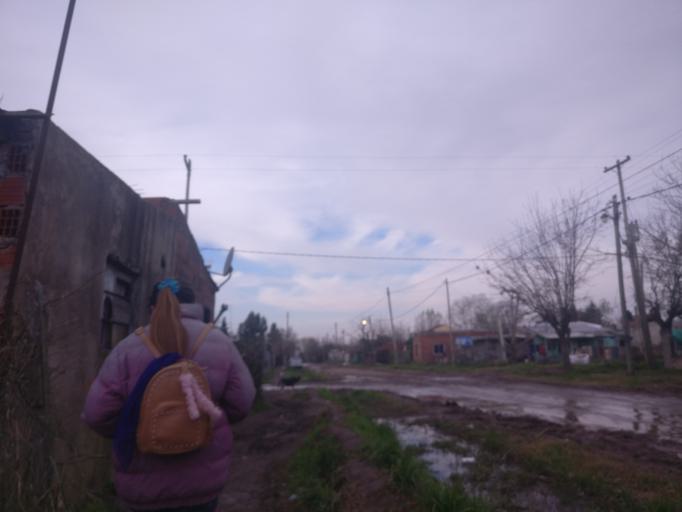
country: AR
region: Buenos Aires
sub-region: Partido de Ezeiza
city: Ezeiza
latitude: -34.9381
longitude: -58.6074
